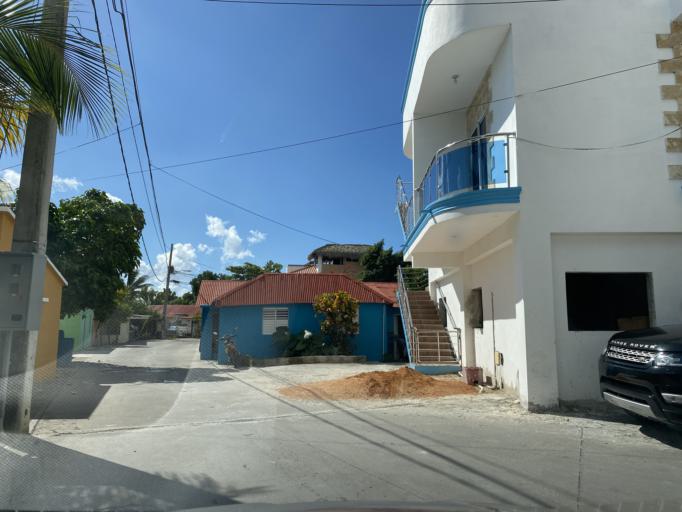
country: DO
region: La Romana
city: La Romana
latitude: 18.3675
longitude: -68.8386
